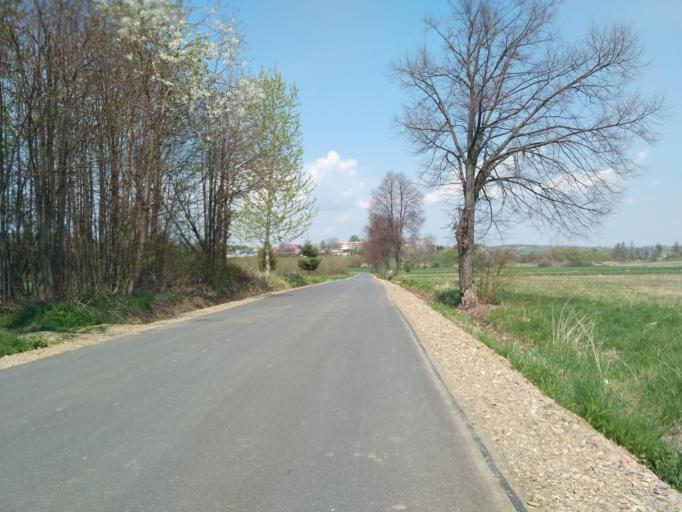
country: PL
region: Subcarpathian Voivodeship
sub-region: Powiat krosnienski
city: Chorkowka
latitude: 49.6423
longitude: 21.6777
